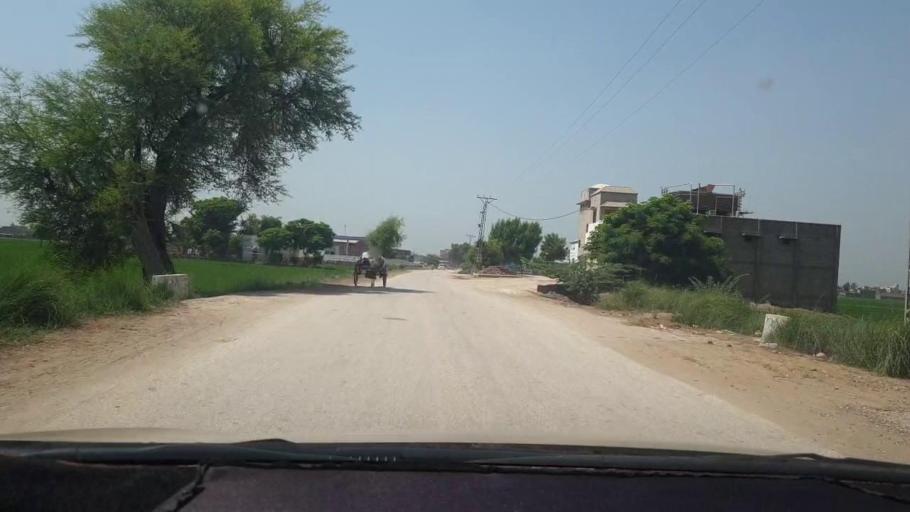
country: PK
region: Sindh
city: Kambar
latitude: 27.5959
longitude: 68.0198
